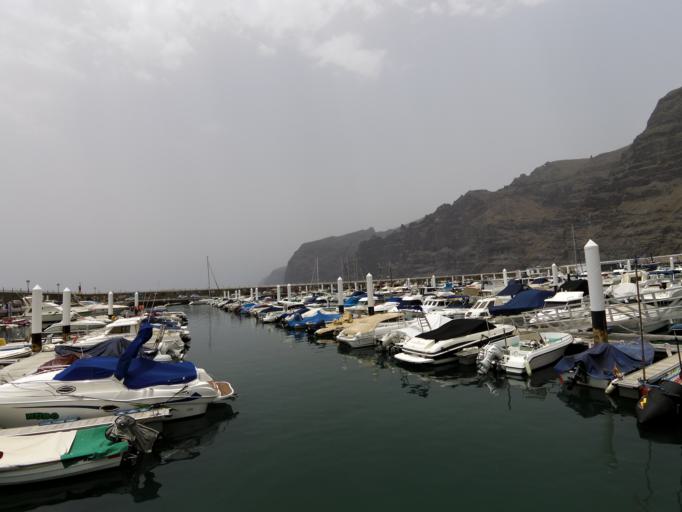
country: ES
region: Canary Islands
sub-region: Provincia de Santa Cruz de Tenerife
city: Santiago del Teide
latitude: 28.2465
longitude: -16.8424
